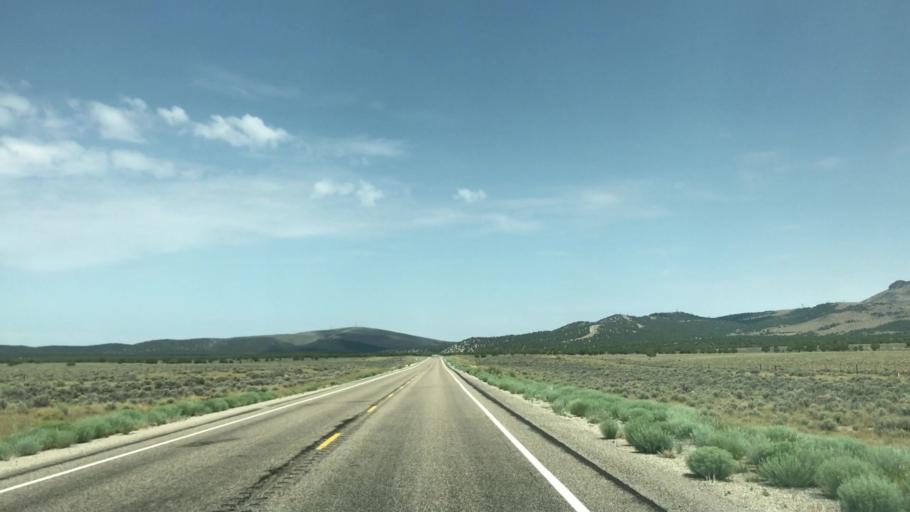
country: US
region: Nevada
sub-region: White Pine County
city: Ely
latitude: 39.3642
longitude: -115.0512
